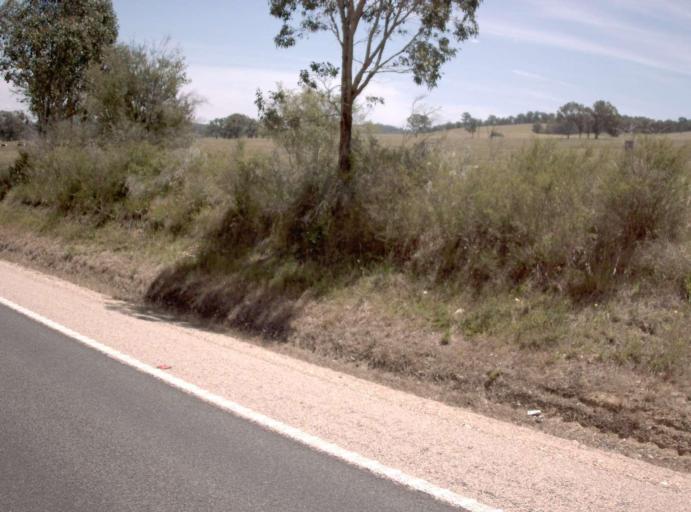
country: AU
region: Victoria
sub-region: East Gippsland
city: Bairnsdale
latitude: -37.7546
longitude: 147.7136
